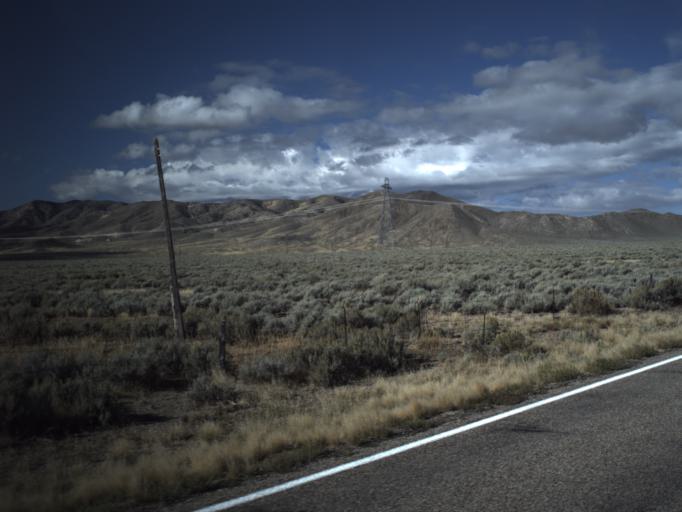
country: US
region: Utah
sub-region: Beaver County
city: Milford
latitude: 38.4093
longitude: -113.0599
